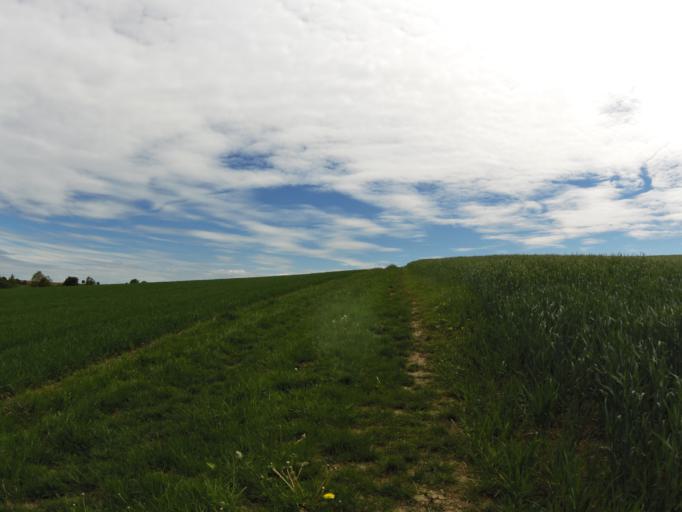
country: DE
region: Bavaria
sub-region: Regierungsbezirk Unterfranken
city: Kurnach
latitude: 49.8418
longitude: 10.0292
